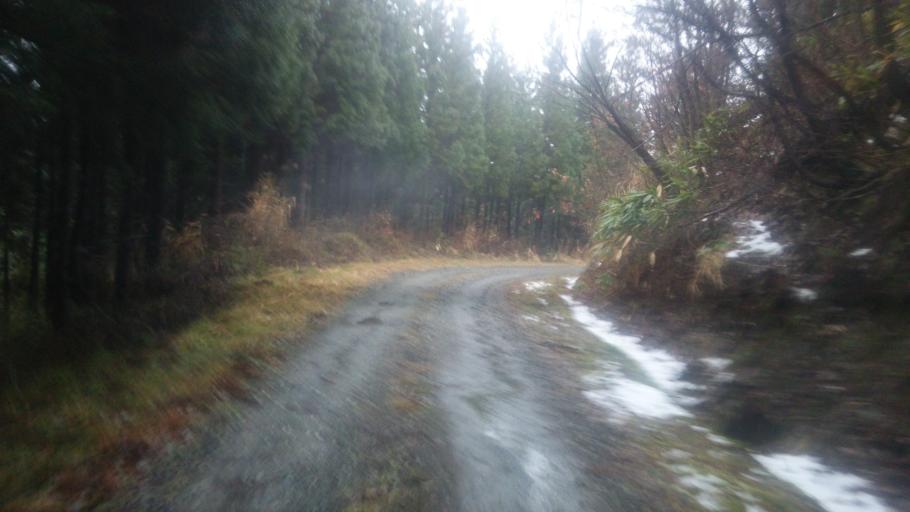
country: JP
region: Fukushima
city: Inawashiro
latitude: 37.5758
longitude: 139.9813
